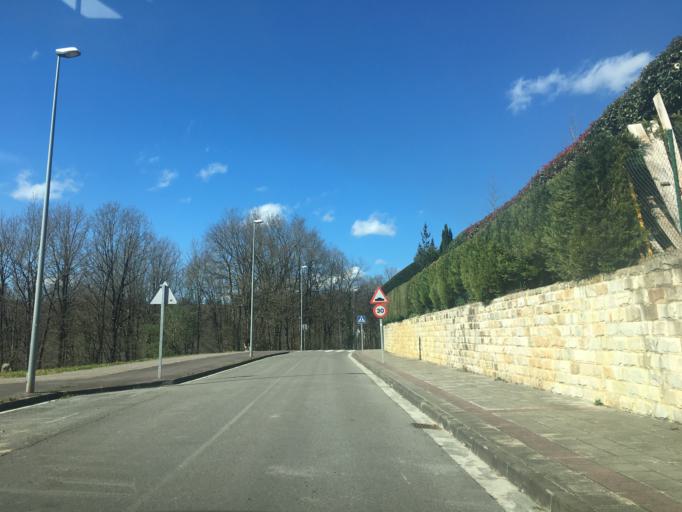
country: ES
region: Basque Country
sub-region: Bizkaia
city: Amorebieta
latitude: 43.2314
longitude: -2.7395
